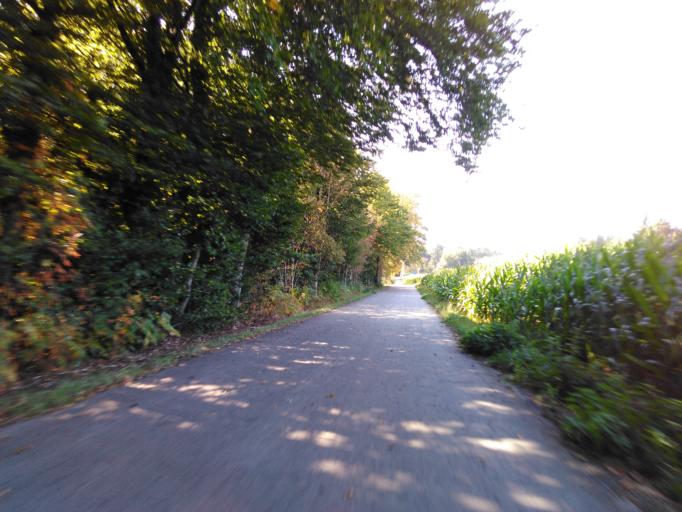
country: LU
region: Diekirch
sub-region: Canton de Redange
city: Rambrouch
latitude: 49.8364
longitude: 5.7923
